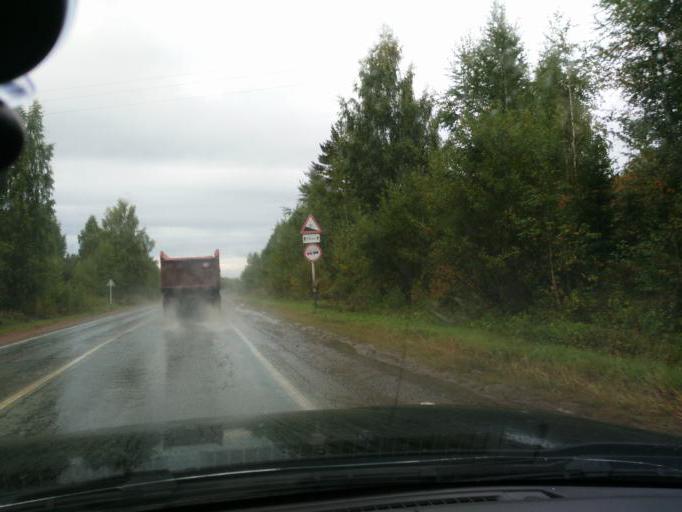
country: RU
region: Perm
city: Kultayevo
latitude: 57.8407
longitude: 55.8252
